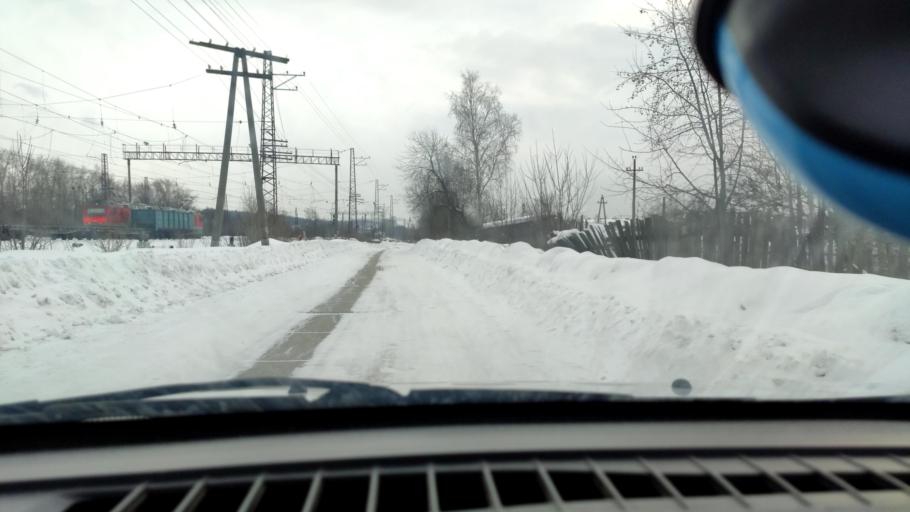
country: RU
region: Perm
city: Overyata
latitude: 58.0843
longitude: 55.8692
